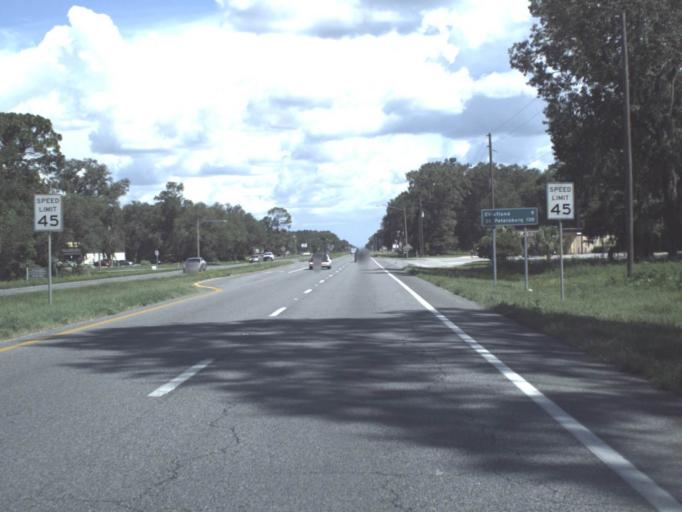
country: US
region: Florida
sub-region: Levy County
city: Manatee Road
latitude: 29.5865
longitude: -82.9224
